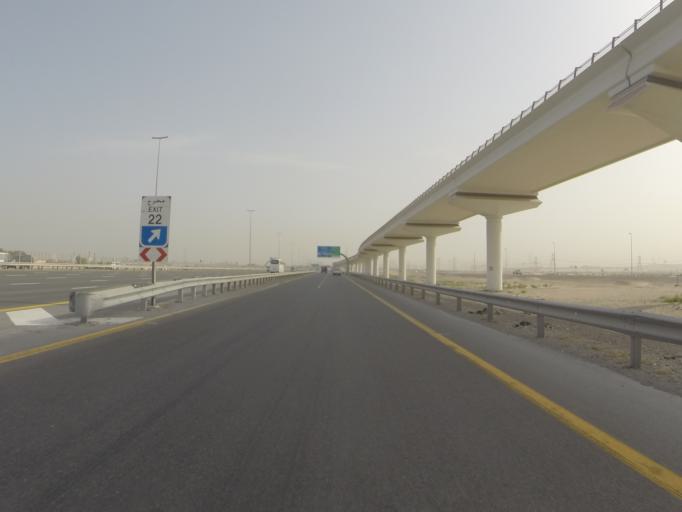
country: AE
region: Dubai
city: Dubai
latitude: 25.0084
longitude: 55.0966
